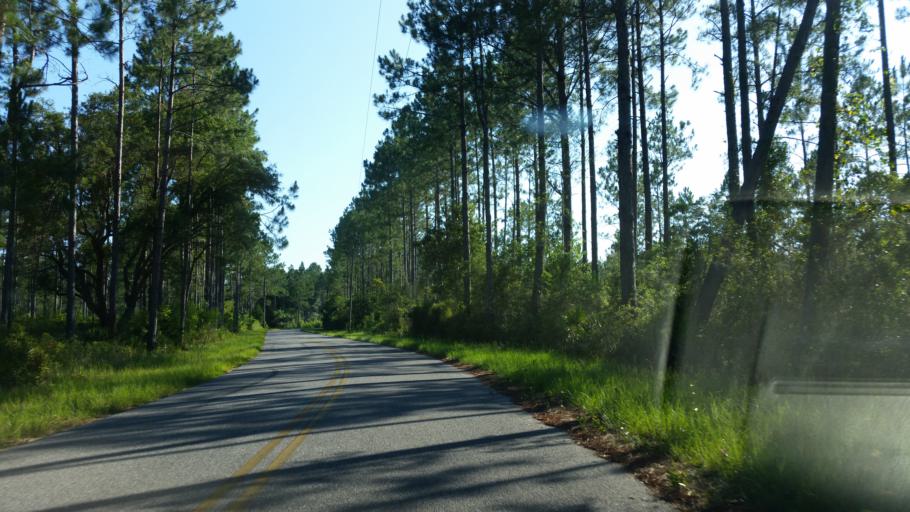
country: US
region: Florida
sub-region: Escambia County
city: Bellview
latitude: 30.4733
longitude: -87.3987
